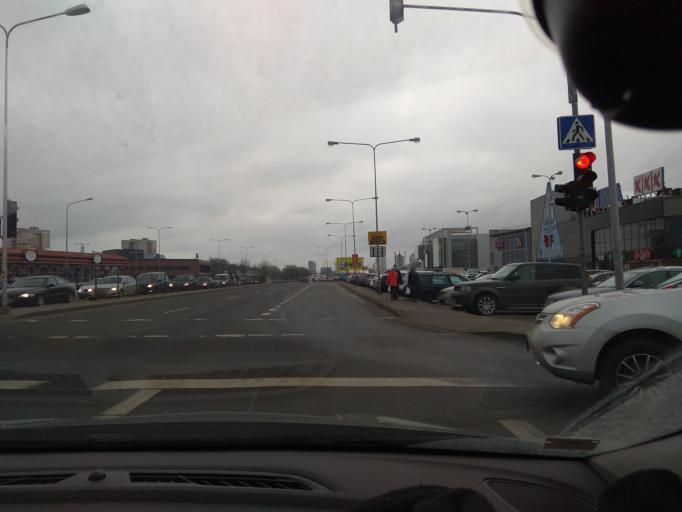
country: LT
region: Vilnius County
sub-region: Vilnius
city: Fabijoniskes
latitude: 54.7287
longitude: 25.2395
